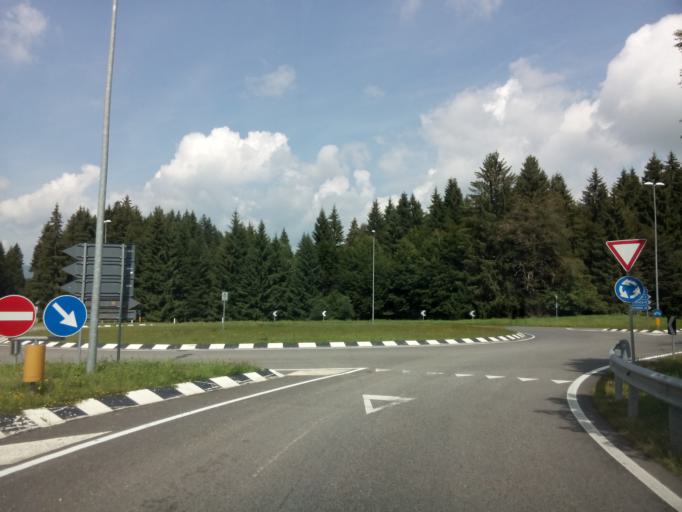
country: IT
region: Veneto
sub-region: Provincia di Vicenza
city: Gallio
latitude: 45.8489
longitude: 11.5472
